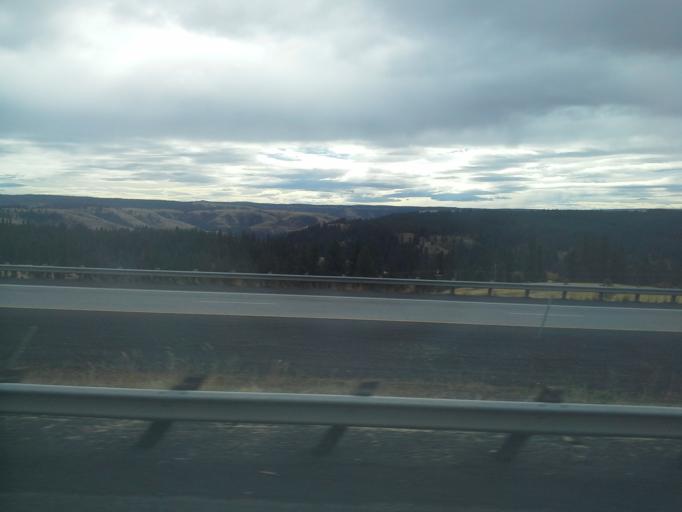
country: US
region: Oregon
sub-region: Umatilla County
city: Mission
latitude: 45.5856
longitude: -118.5755
